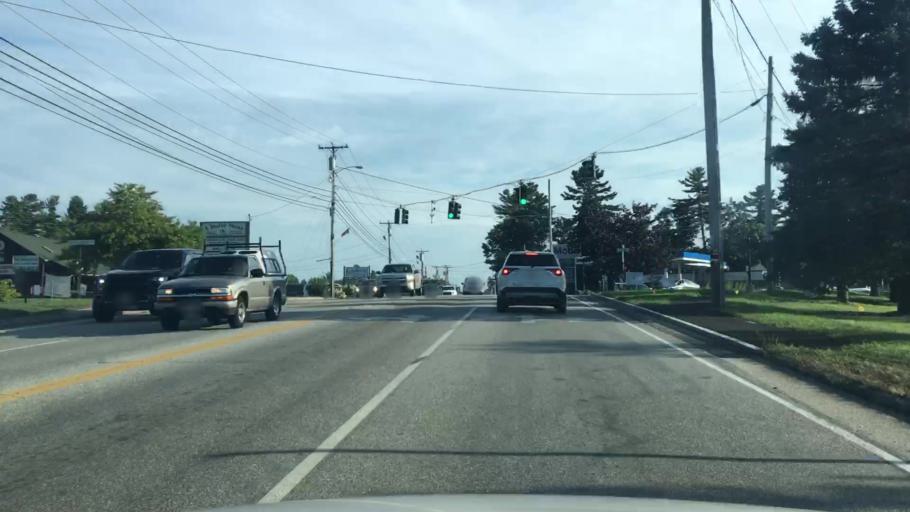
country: US
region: Maine
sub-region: Cumberland County
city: North Windham
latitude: 43.8282
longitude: -70.4348
